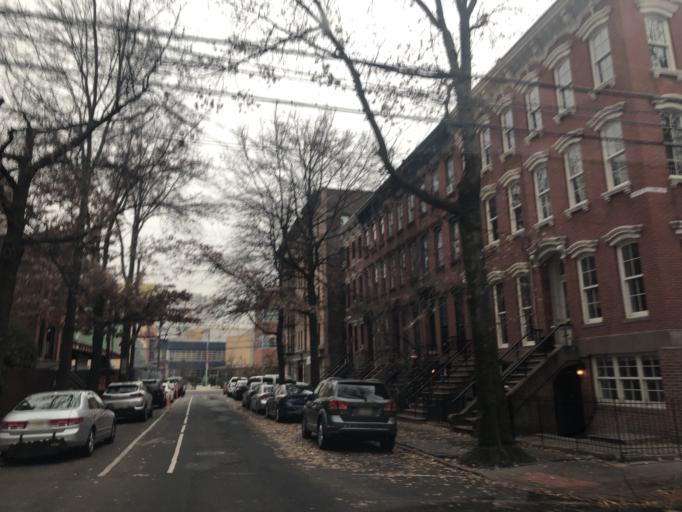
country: US
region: New Jersey
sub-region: Hudson County
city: Jersey City
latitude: 40.7175
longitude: -74.0500
